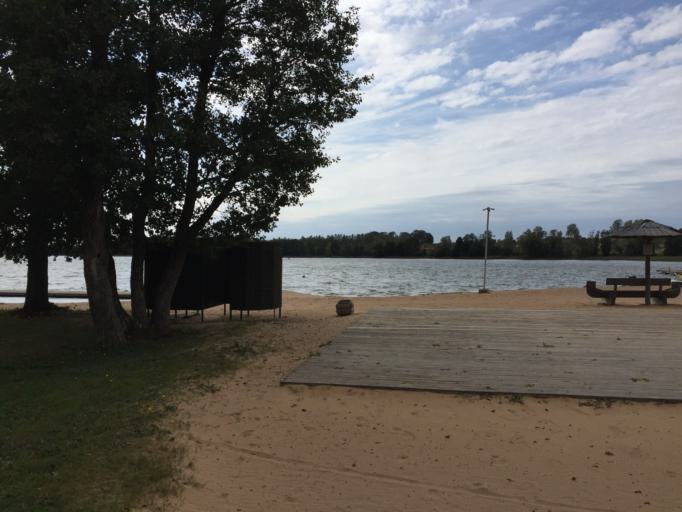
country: LV
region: Limbazu Rajons
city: Limbazi
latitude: 57.5033
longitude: 24.7035
